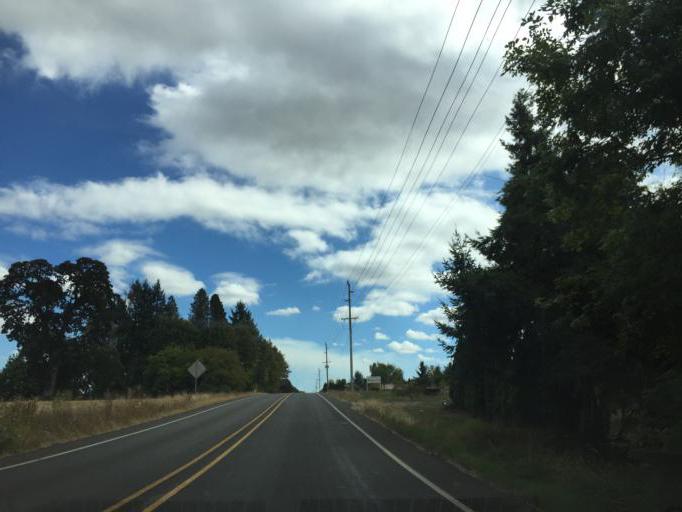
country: US
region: Oregon
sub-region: Marion County
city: Mount Angel
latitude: 45.1196
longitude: -122.8003
